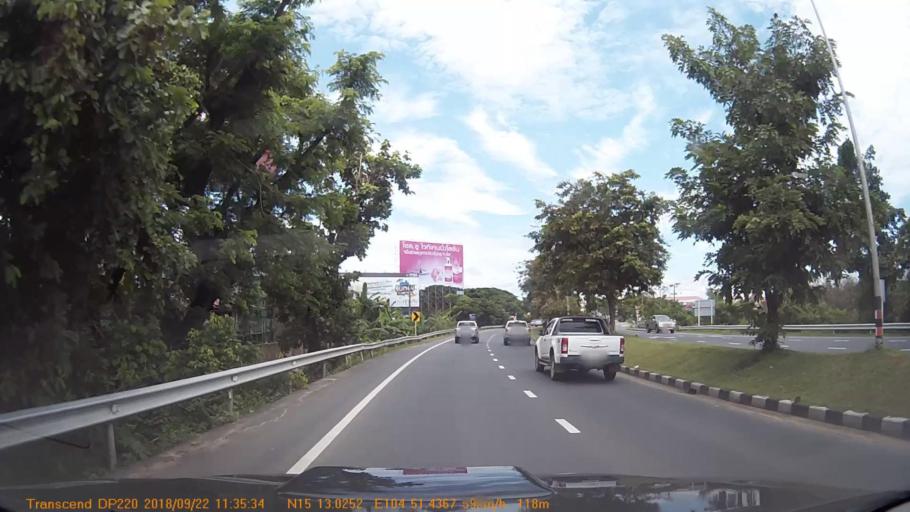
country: TH
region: Changwat Ubon Ratchathani
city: Ubon Ratchathani
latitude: 15.2170
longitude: 104.8573
